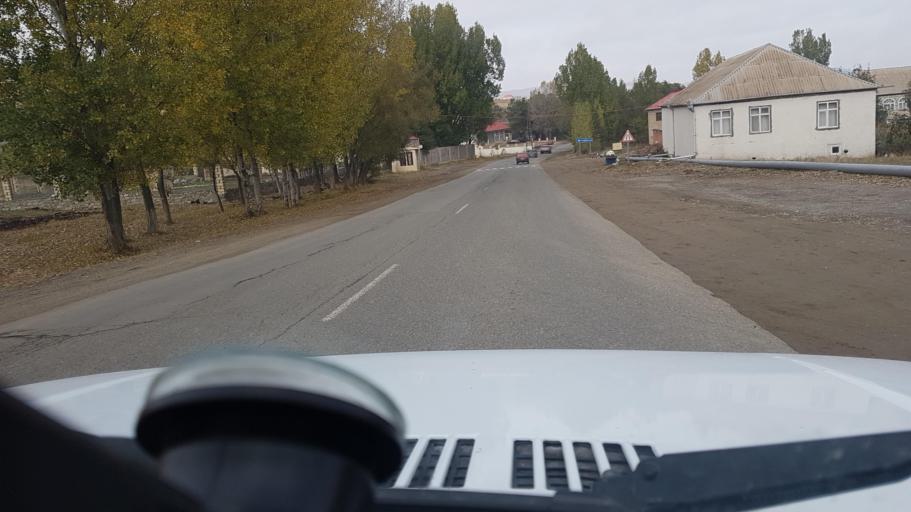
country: AZ
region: Gadabay Rayon
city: Ariqdam
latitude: 40.6325
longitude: 45.8136
